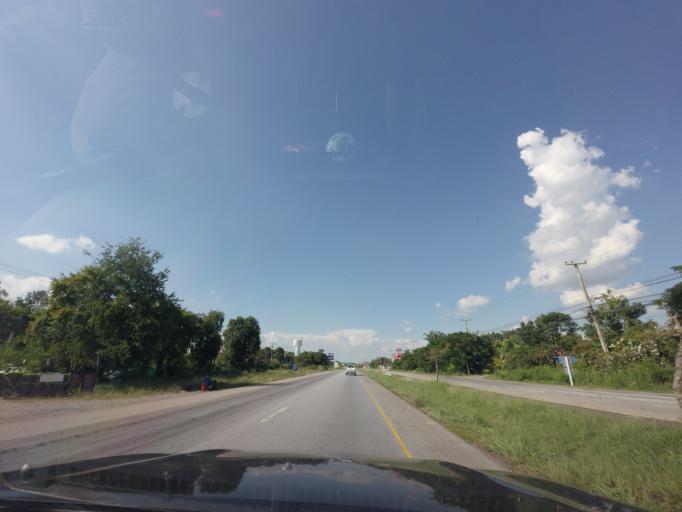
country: TH
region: Nakhon Ratchasima
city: Sida
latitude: 15.5412
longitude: 102.5465
